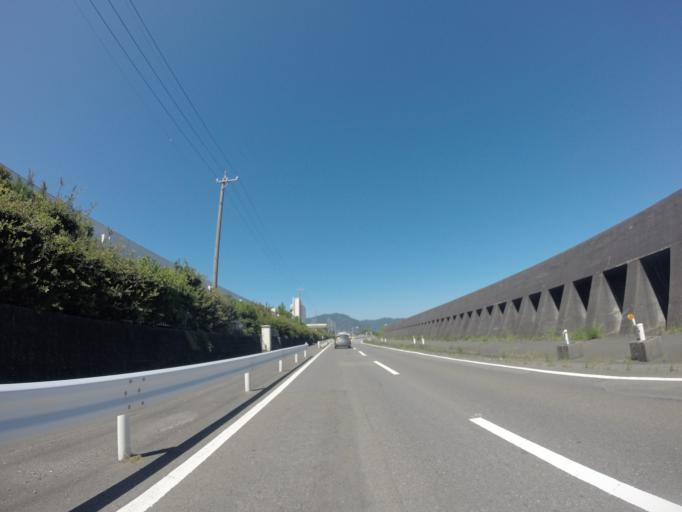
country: JP
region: Shizuoka
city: Yaizu
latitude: 34.8512
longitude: 138.3241
